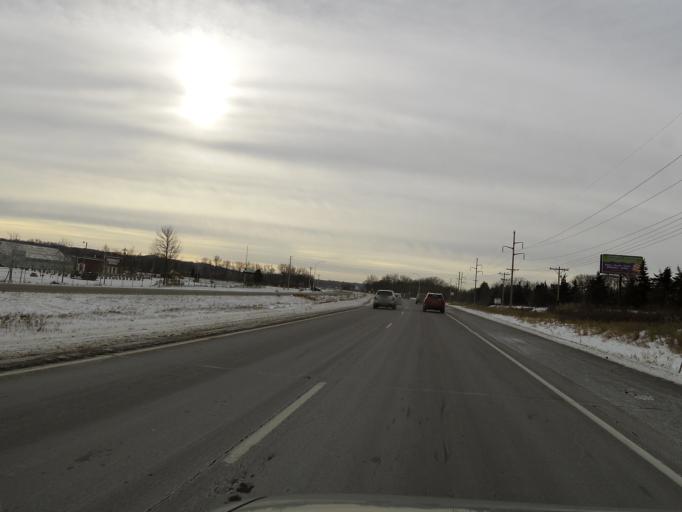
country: US
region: Minnesota
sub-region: Carver County
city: Carver
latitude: 44.7349
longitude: -93.5888
